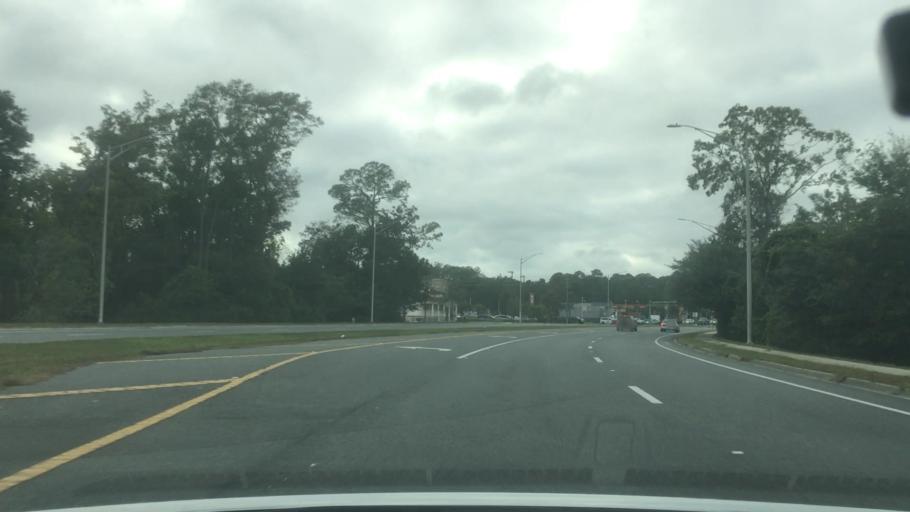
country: US
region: Florida
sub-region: Duval County
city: Jacksonville
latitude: 30.4755
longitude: -81.6275
